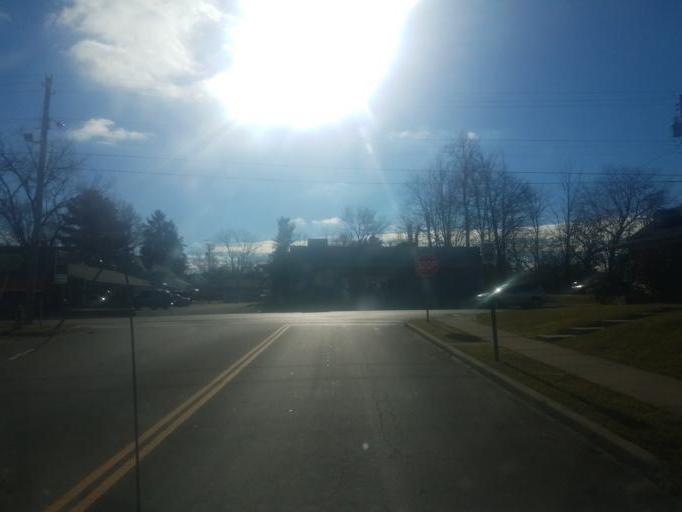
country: US
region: Ohio
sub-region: Richland County
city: Mansfield
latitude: 40.7538
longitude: -82.5236
